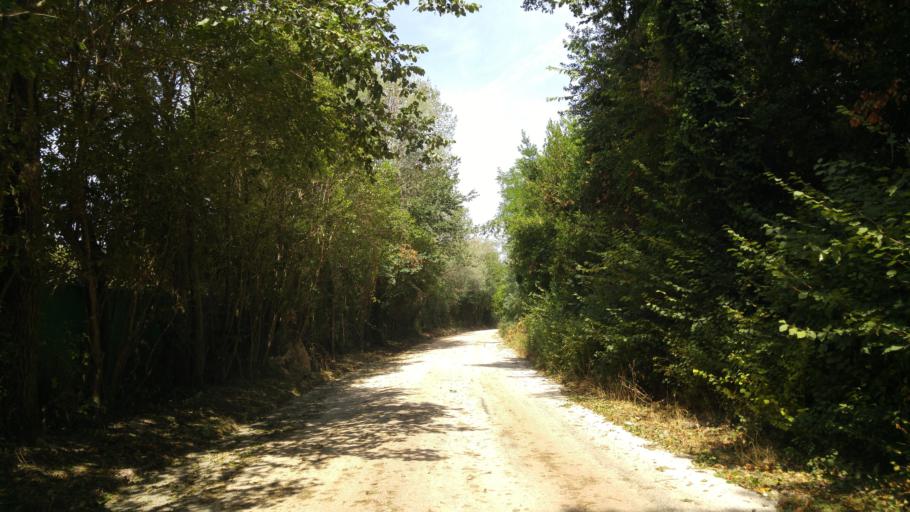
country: IT
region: The Marches
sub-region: Provincia di Pesaro e Urbino
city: Centinarola
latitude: 43.8521
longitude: 12.9958
